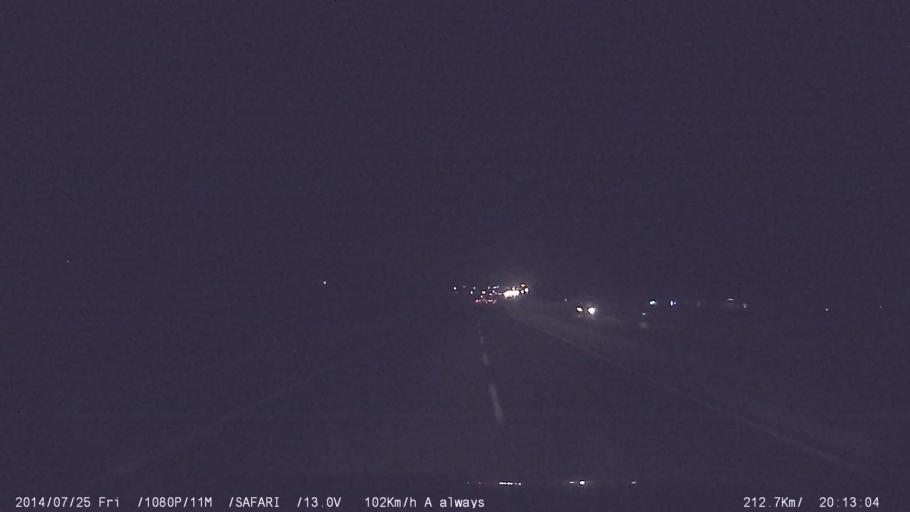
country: IN
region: Tamil Nadu
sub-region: Salem
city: Attayyampatti
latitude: 11.5628
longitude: 78.0238
